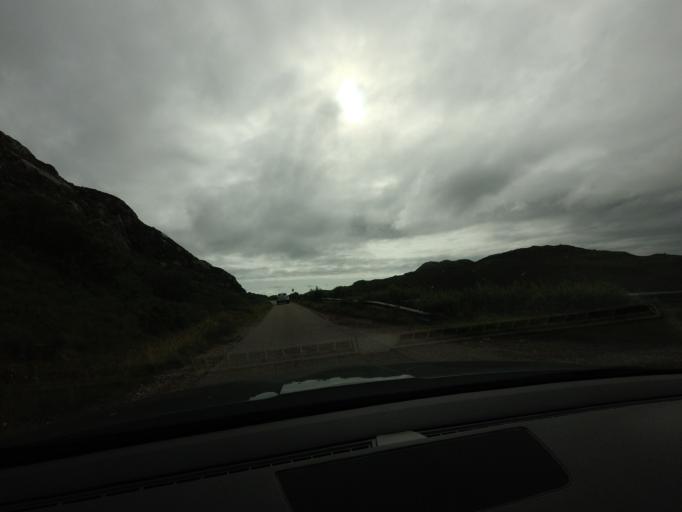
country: GB
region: Scotland
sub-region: Highland
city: Ullapool
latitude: 58.4357
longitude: -4.9663
